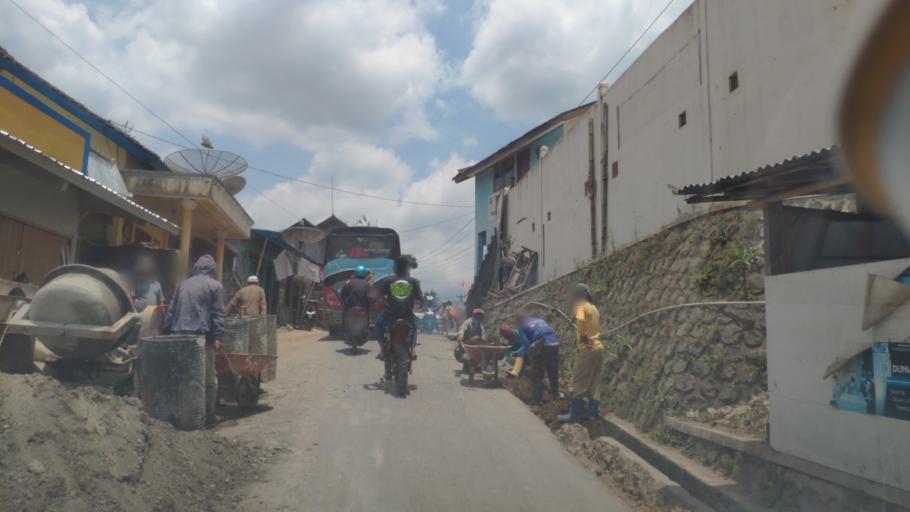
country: ID
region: Central Java
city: Wonosobo
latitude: -7.3024
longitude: 109.8082
